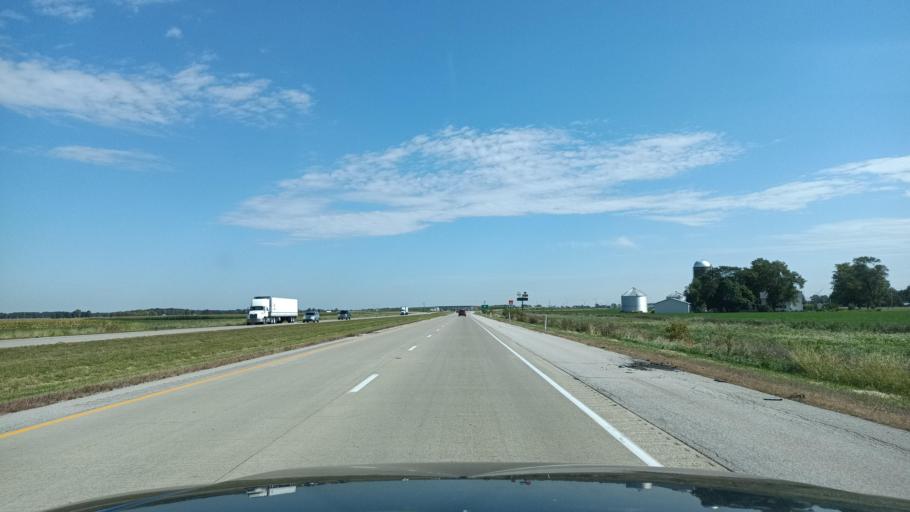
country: US
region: Indiana
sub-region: Allen County
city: Woodburn
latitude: 41.1400
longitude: -84.8610
